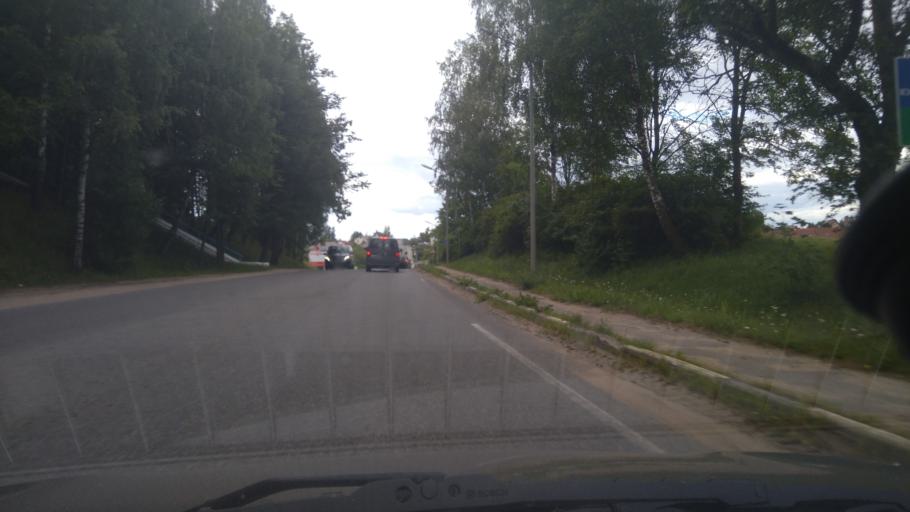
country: BY
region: Minsk
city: Zhdanovichy
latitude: 53.9127
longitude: 27.3915
